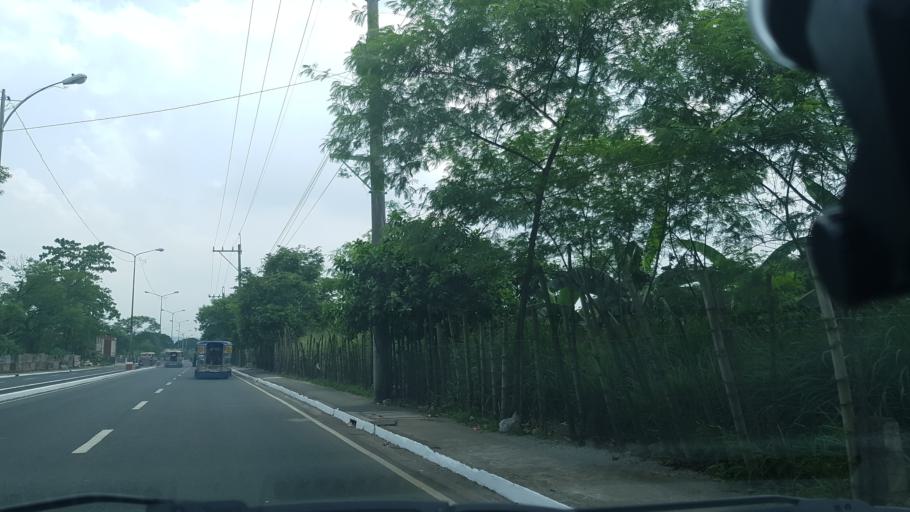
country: PH
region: Calabarzon
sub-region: Province of Rizal
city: San Mateo
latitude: 14.6825
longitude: 121.1066
